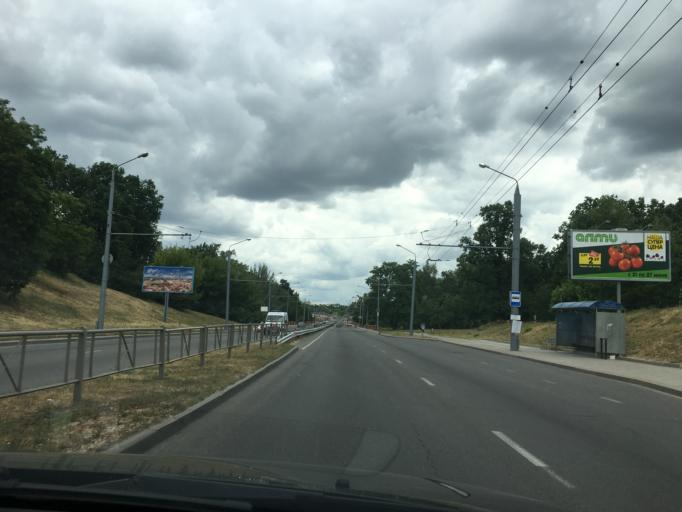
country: BY
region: Grodnenskaya
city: Hrodna
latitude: 53.6568
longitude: 23.8579
